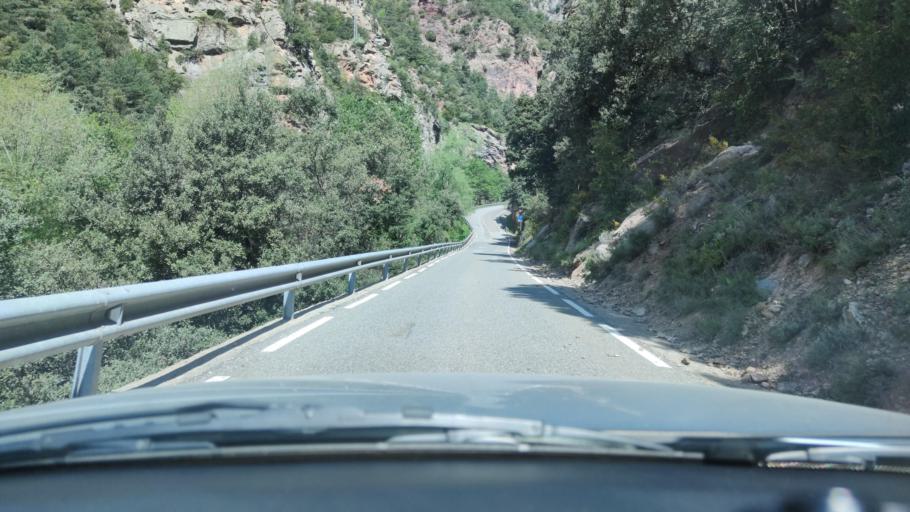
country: ES
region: Catalonia
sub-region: Provincia de Lleida
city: Coll de Nargo
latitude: 42.3038
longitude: 1.2912
